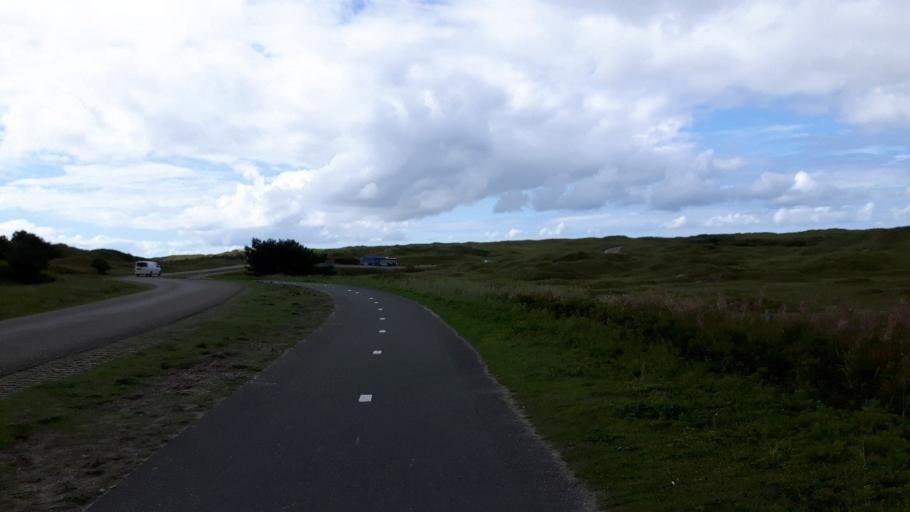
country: NL
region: Friesland
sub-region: Gemeente Ameland
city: Hollum
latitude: 53.4493
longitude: 5.6237
